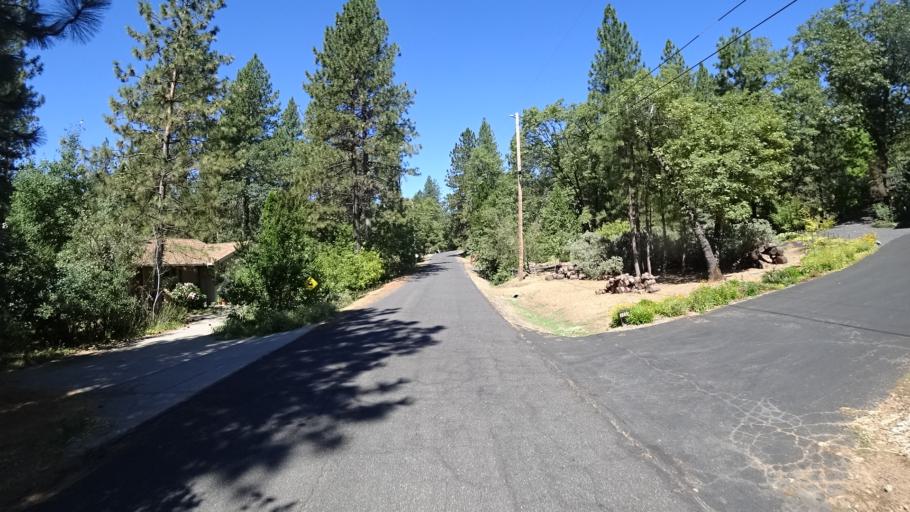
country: US
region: California
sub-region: Calaveras County
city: Forest Meadows
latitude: 38.1822
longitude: -120.3656
